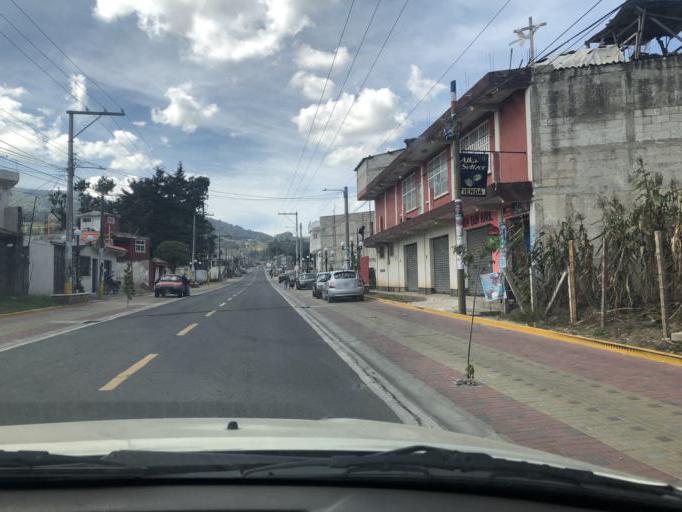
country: GT
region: Quetzaltenango
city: San Mateo
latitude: 14.8628
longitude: -91.5844
